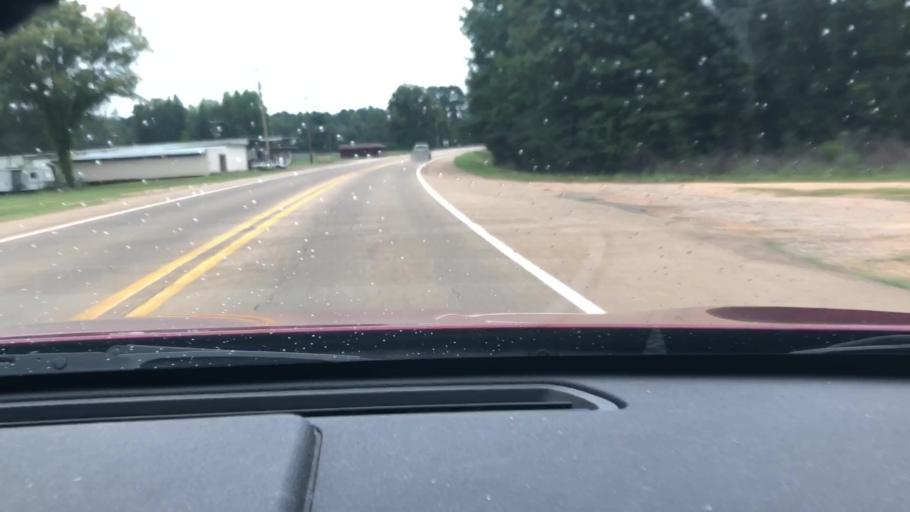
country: US
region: Arkansas
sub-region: Lafayette County
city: Stamps
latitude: 33.3675
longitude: -93.5149
